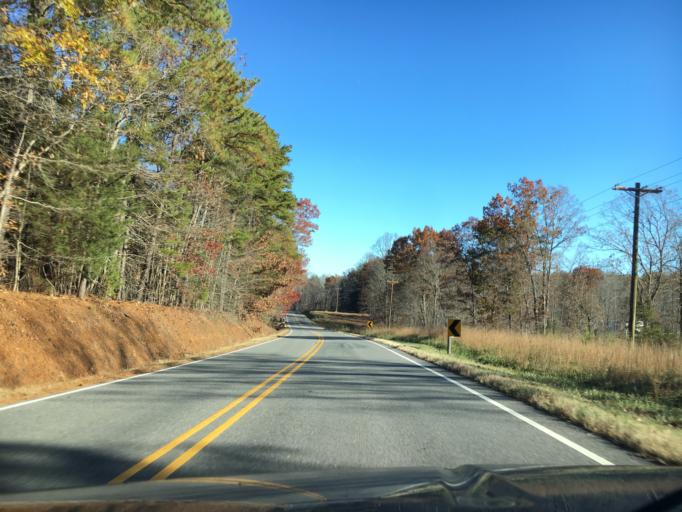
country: US
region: Virginia
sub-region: Buckingham County
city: Buckingham
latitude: 37.4686
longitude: -78.6623
